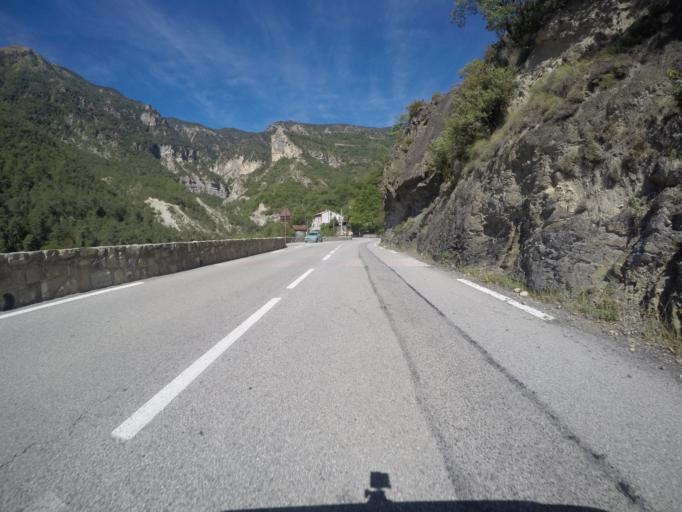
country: FR
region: Provence-Alpes-Cote d'Azur
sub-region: Departement des Alpes-Maritimes
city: Gilette
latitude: 43.9725
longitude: 7.1455
